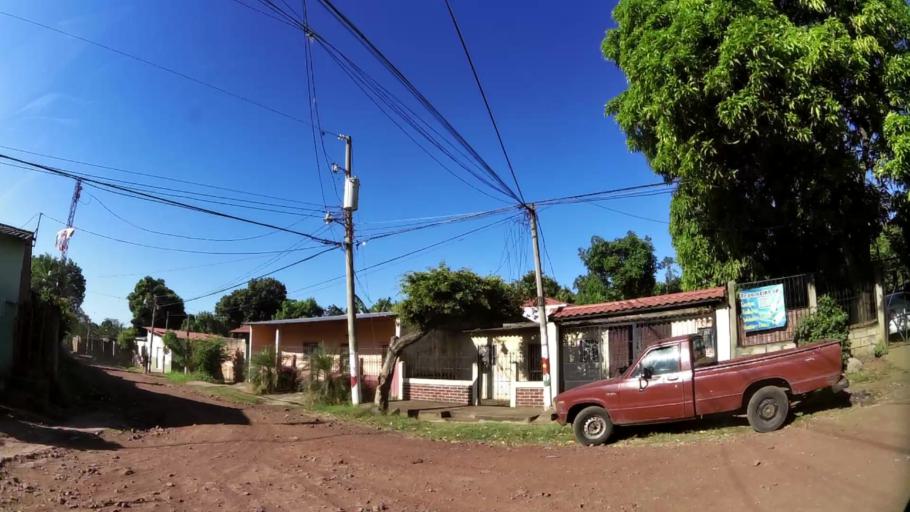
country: SV
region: Sonsonate
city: Sonzacate
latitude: 13.7416
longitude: -89.7102
